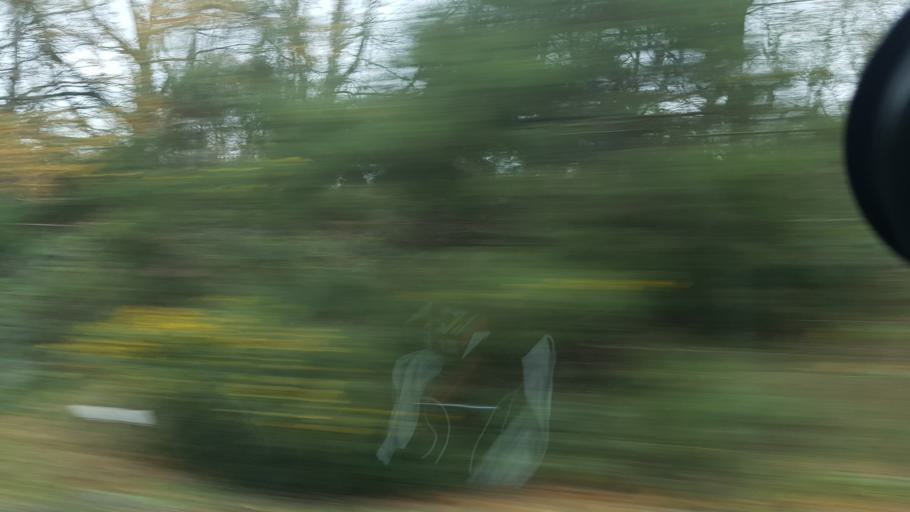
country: GB
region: England
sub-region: Hampshire
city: Yateley
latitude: 51.3229
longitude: -0.8324
